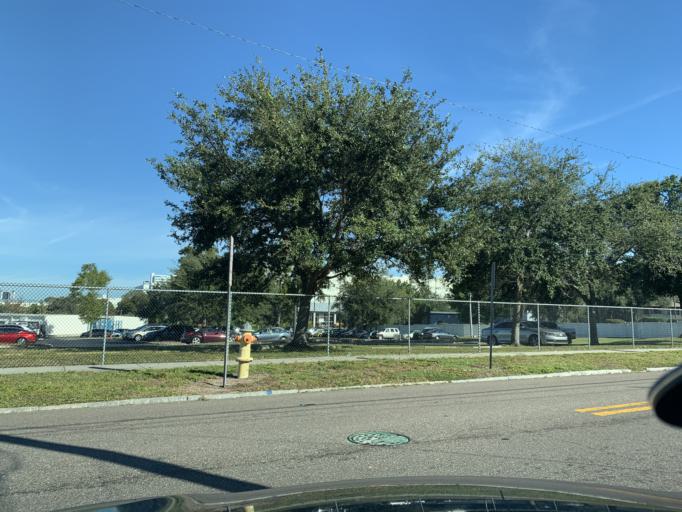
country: US
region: Florida
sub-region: Pinellas County
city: Saint Petersburg
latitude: 27.7630
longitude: -82.6487
